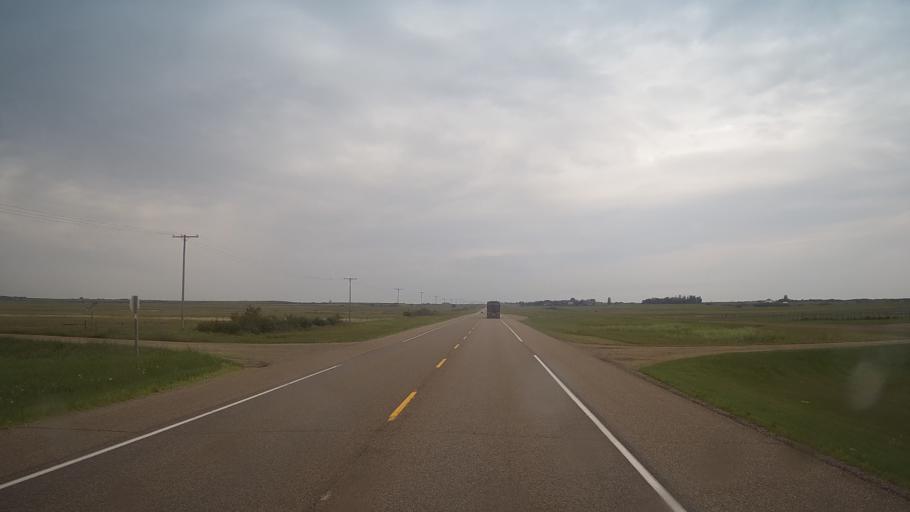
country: CA
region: Saskatchewan
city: Langham
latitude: 52.1289
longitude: -107.1455
